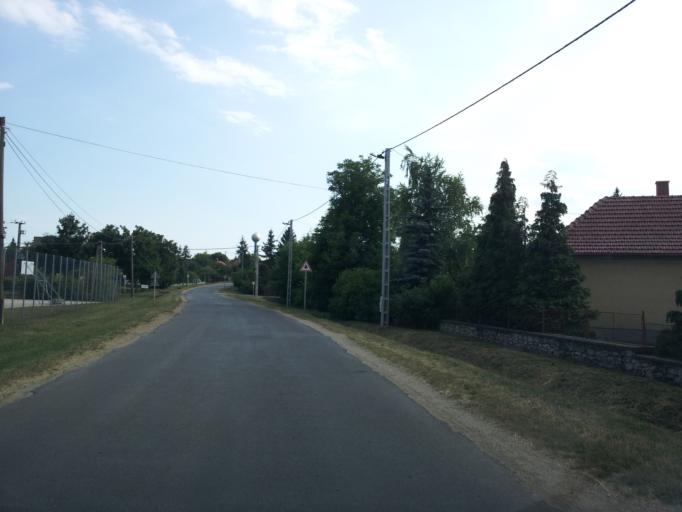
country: HU
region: Veszprem
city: Zanka
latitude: 46.9813
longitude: 17.6929
